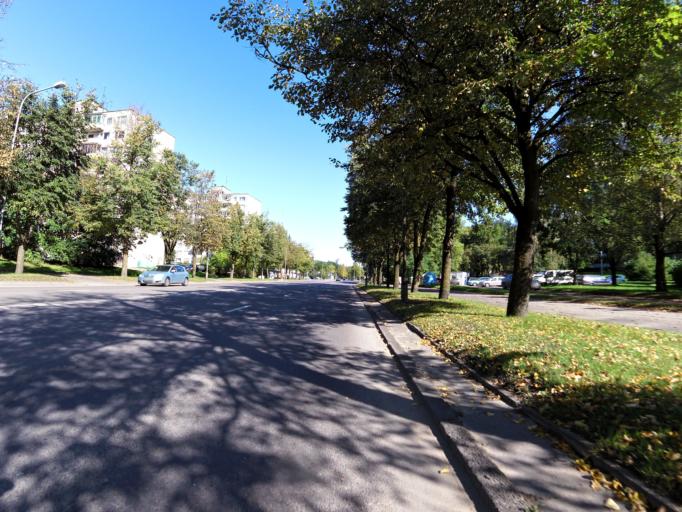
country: LT
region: Vilnius County
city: Lazdynai
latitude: 54.6729
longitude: 25.1999
